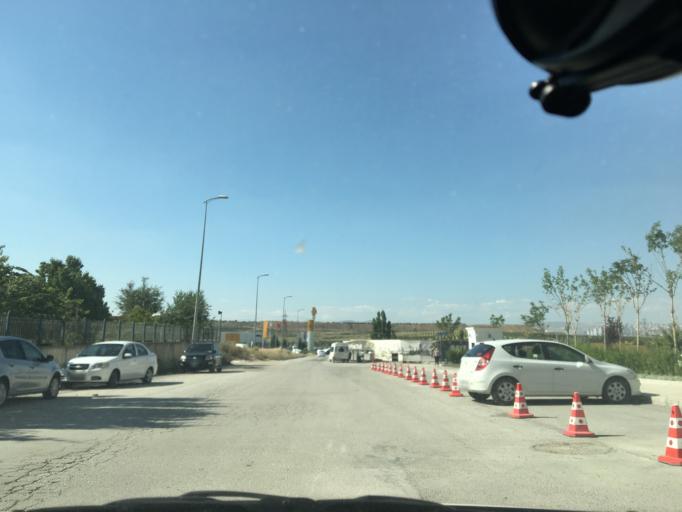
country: TR
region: Ankara
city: Batikent
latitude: 39.9085
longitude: 32.7434
